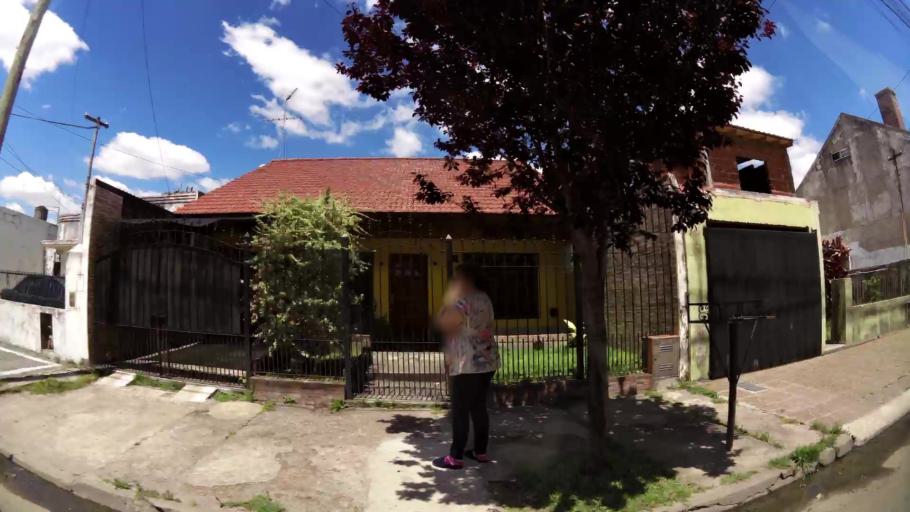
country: AR
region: Buenos Aires
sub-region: Partido de Lanus
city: Lanus
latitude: -34.7226
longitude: -58.4120
